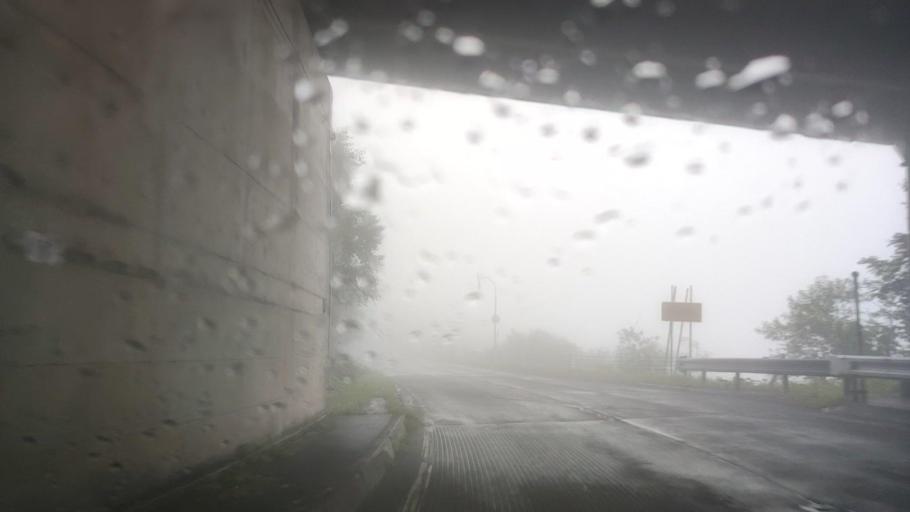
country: JP
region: Hokkaido
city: Date
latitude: 42.5491
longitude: 141.0881
